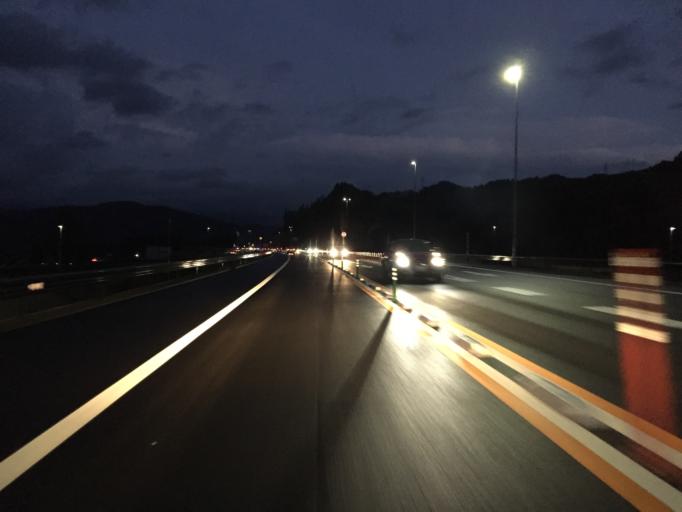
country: JP
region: Yamagata
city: Yonezawa
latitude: 37.8952
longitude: 140.1540
